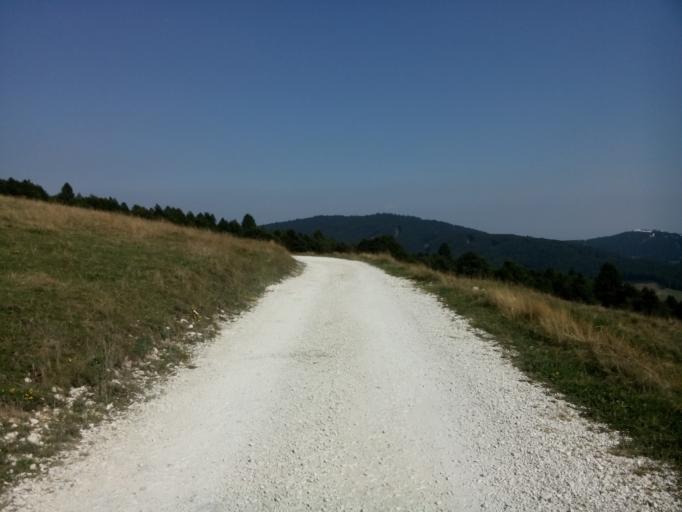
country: IT
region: Veneto
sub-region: Provincia di Vicenza
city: Conco
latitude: 45.8312
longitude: 11.6149
